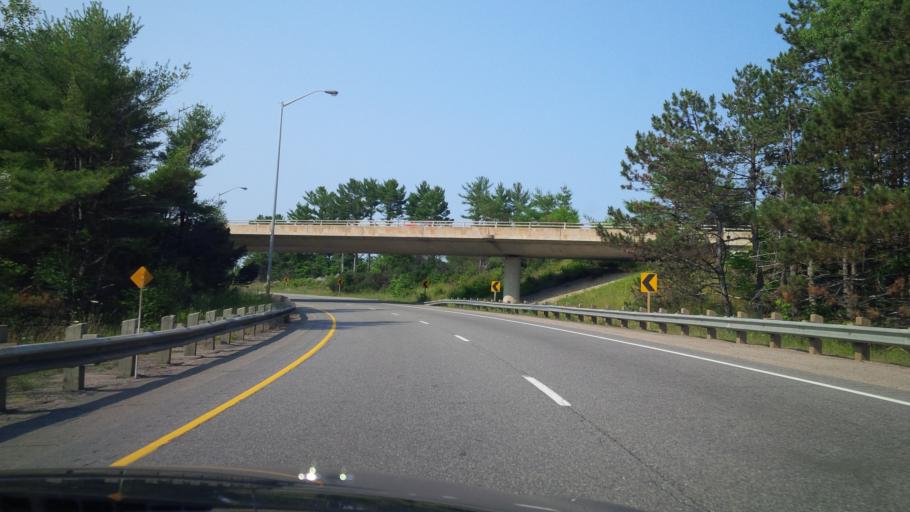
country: CA
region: Ontario
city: Gravenhurst
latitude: 44.9058
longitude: -79.3665
